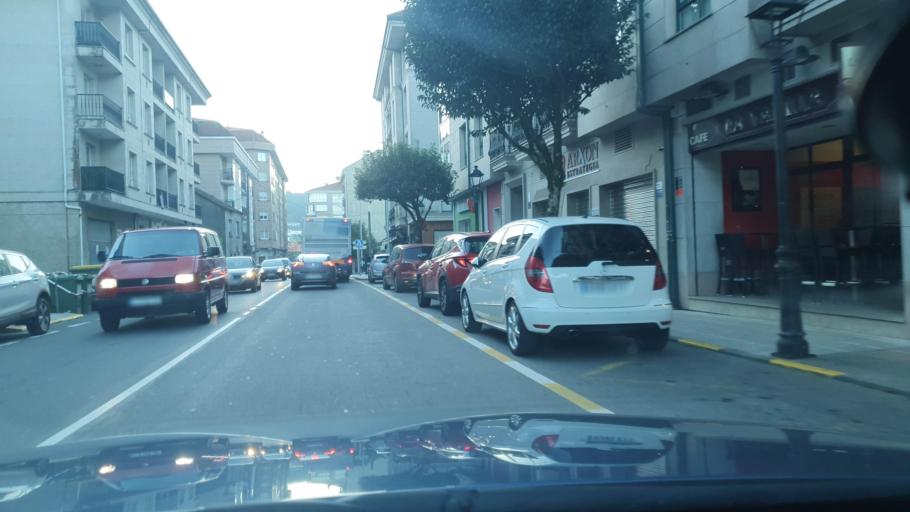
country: ES
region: Galicia
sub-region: Provincia da Coruna
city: Santiago de Compostela
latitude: 42.8430
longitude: -8.5805
